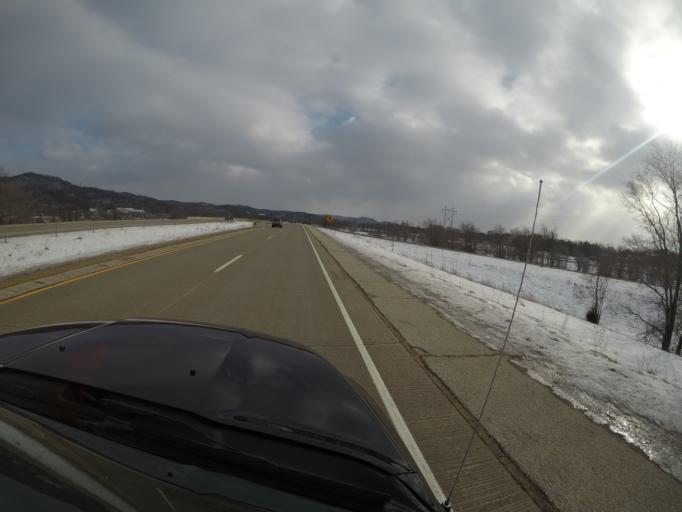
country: US
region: Wisconsin
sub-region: La Crosse County
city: Holmen
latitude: 43.9429
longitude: -91.2585
